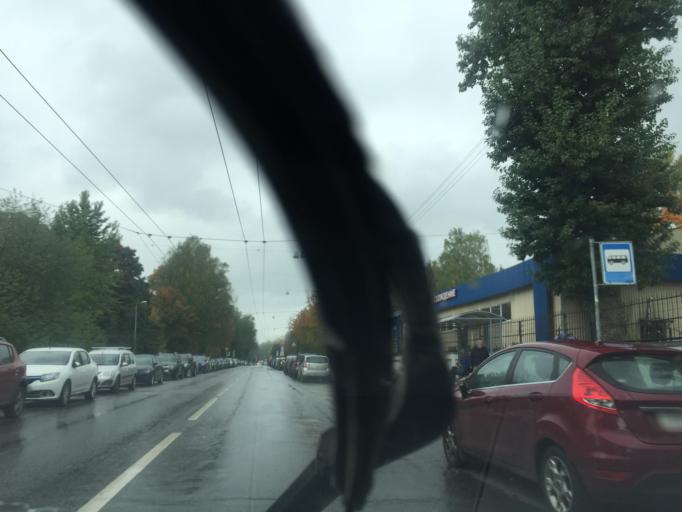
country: RU
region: St.-Petersburg
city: Sosnovka
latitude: 60.0092
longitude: 30.3604
